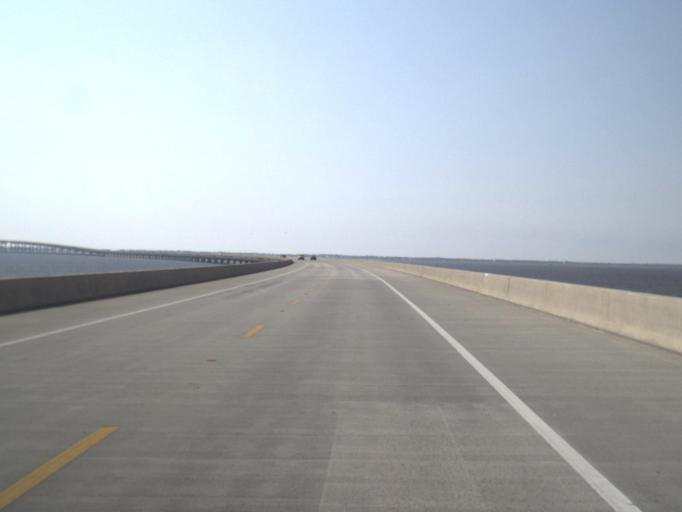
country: US
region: Florida
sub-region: Franklin County
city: Eastpoint
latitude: 29.7019
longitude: -84.8904
